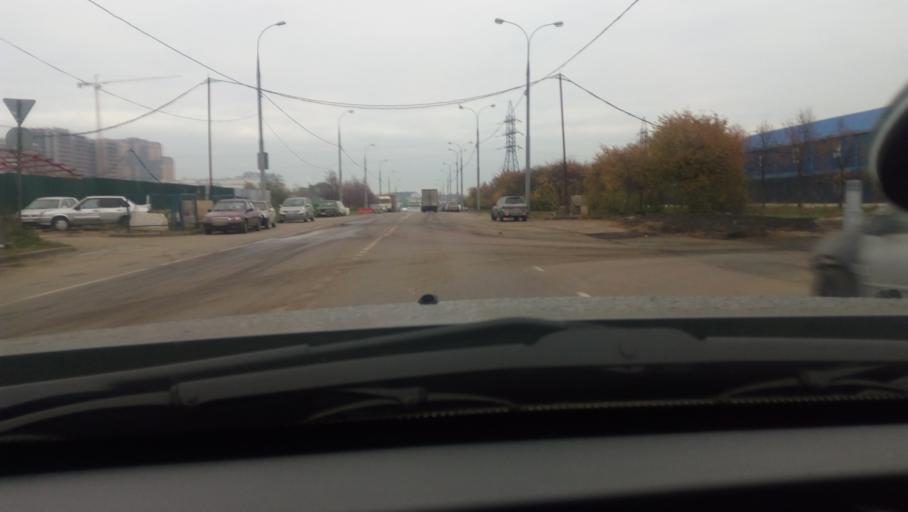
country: RU
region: Moskovskaya
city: Reutov
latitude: 55.7456
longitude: 37.8834
